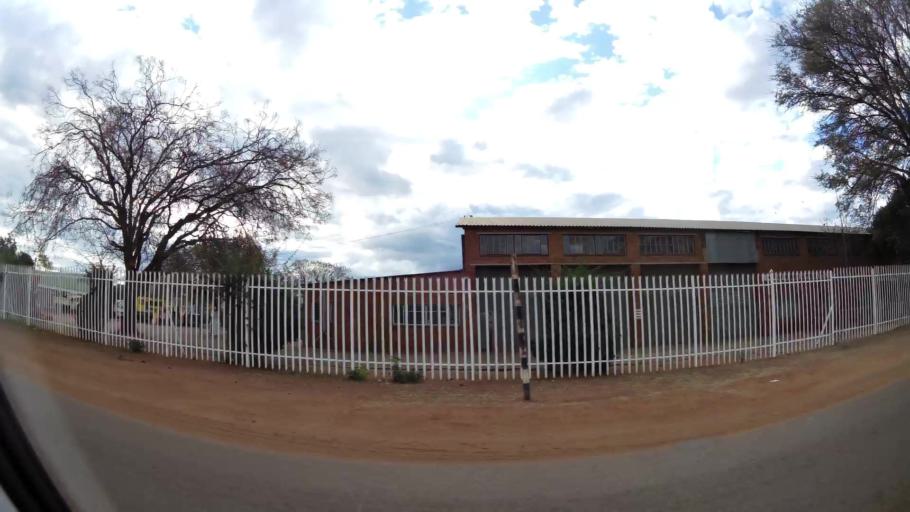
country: ZA
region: Limpopo
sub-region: Waterberg District Municipality
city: Modimolle
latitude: -24.5197
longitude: 28.7175
